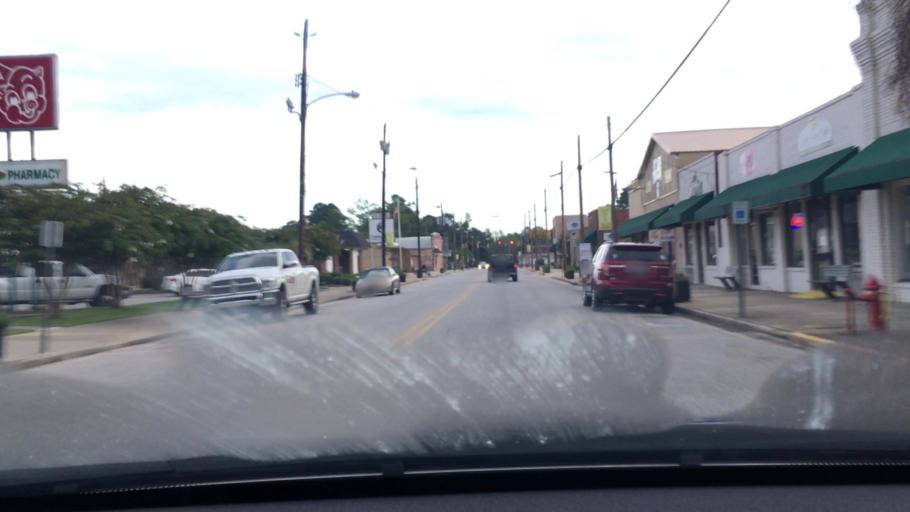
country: US
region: South Carolina
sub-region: Florence County
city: Timmonsville
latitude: 34.1702
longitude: -80.0641
